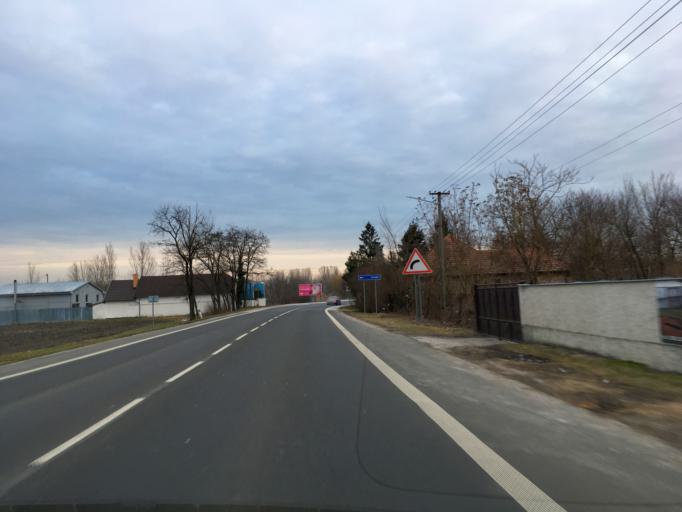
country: SK
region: Trnavsky
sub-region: Okres Dunajska Streda
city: Velky Meder
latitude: 47.9441
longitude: 17.7160
